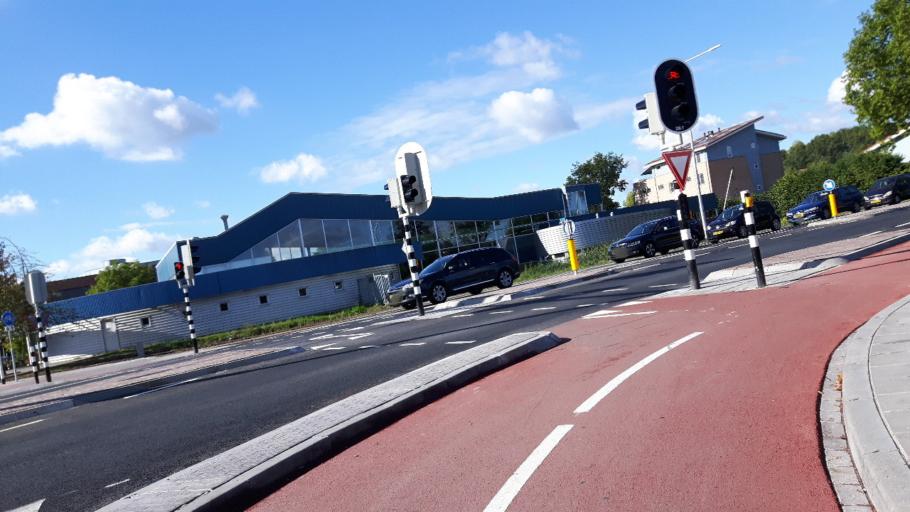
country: NL
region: Gelderland
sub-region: Gemeente Culemborg
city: Culemborg
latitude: 51.9470
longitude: 5.2372
